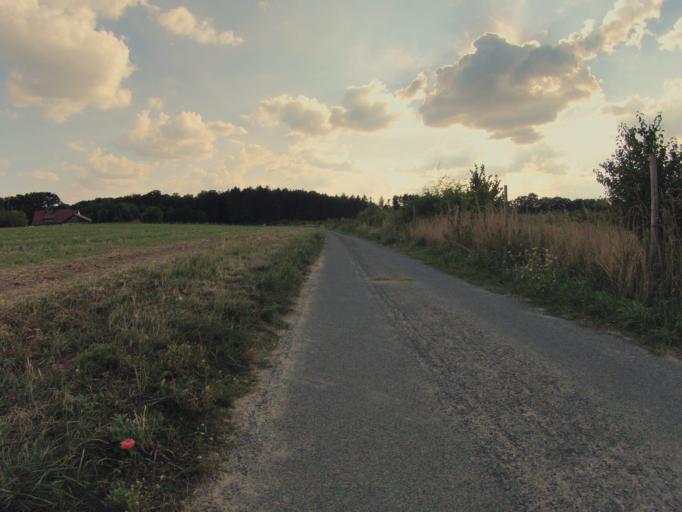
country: DE
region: North Rhine-Westphalia
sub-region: Regierungsbezirk Munster
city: Tecklenburg
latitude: 52.2660
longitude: 7.8189
